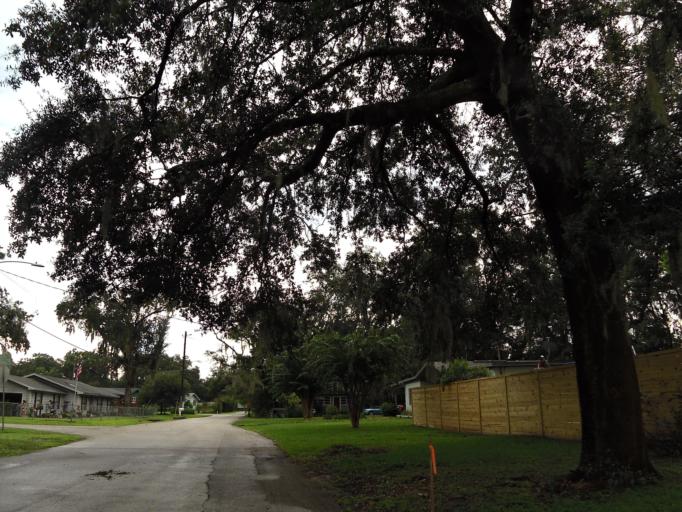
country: US
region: Florida
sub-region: Duval County
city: Jacksonville
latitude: 30.2976
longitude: -81.5992
